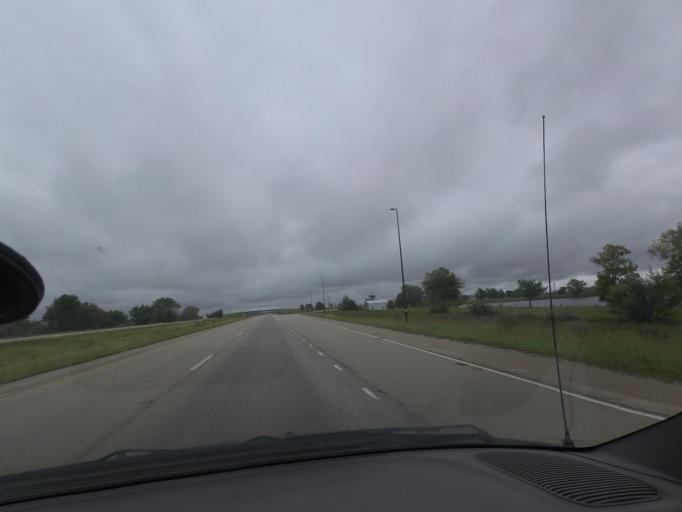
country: US
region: Illinois
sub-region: Piatt County
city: Cerro Gordo
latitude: 39.9505
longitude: -88.8264
